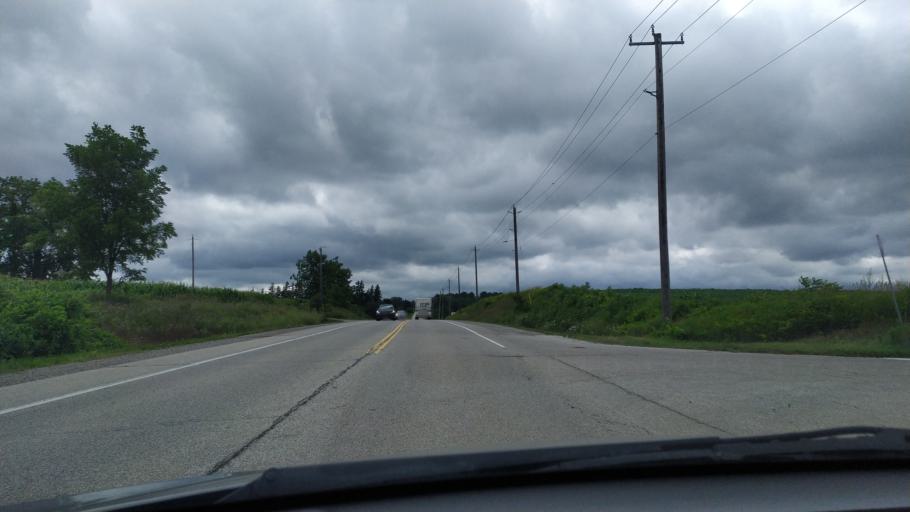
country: CA
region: Ontario
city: Kitchener
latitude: 43.3652
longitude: -80.4390
